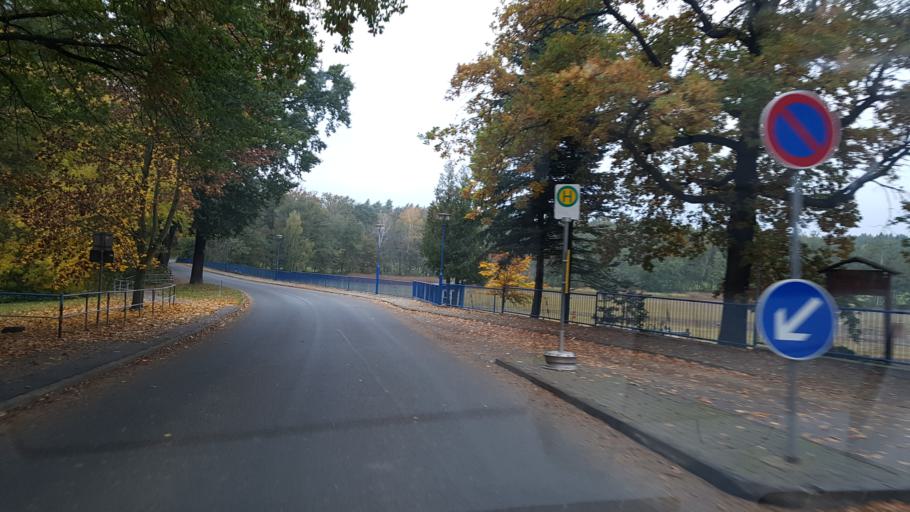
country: DE
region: Saxony
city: Dahlen
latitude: 51.3945
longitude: 13.0040
